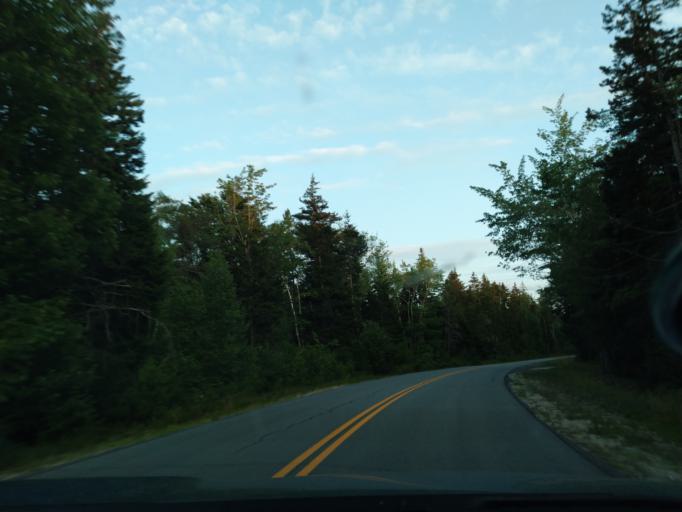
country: US
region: Maine
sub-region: Hancock County
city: Gouldsboro
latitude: 44.3885
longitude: -68.0707
